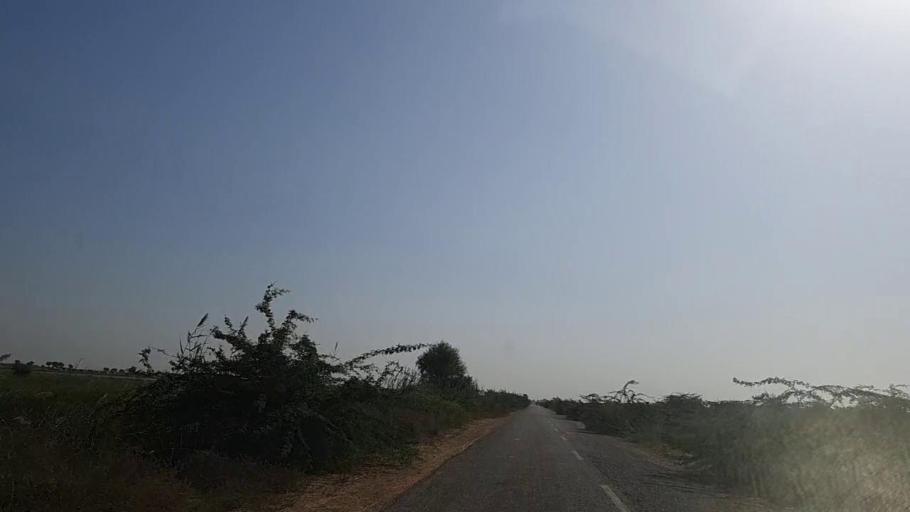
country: PK
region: Sindh
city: Jati
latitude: 24.4415
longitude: 68.2614
